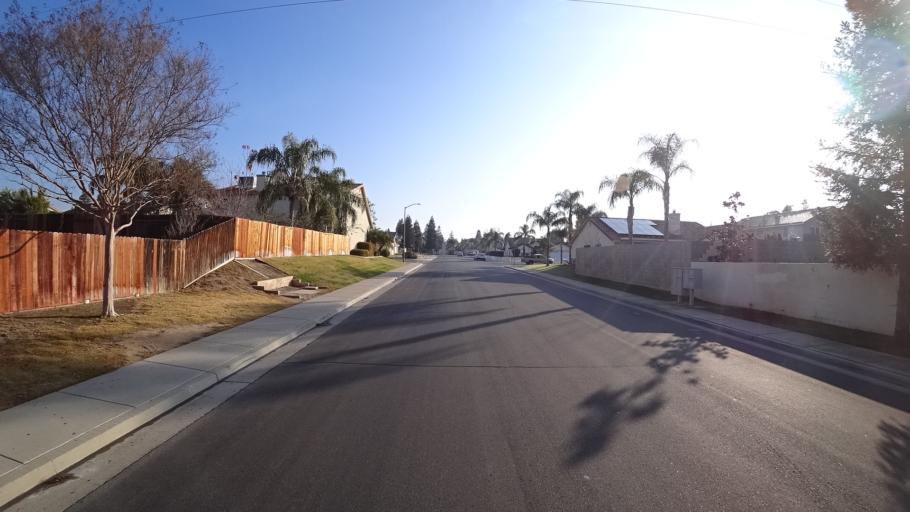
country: US
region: California
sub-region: Kern County
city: Oildale
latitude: 35.4034
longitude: -118.9404
